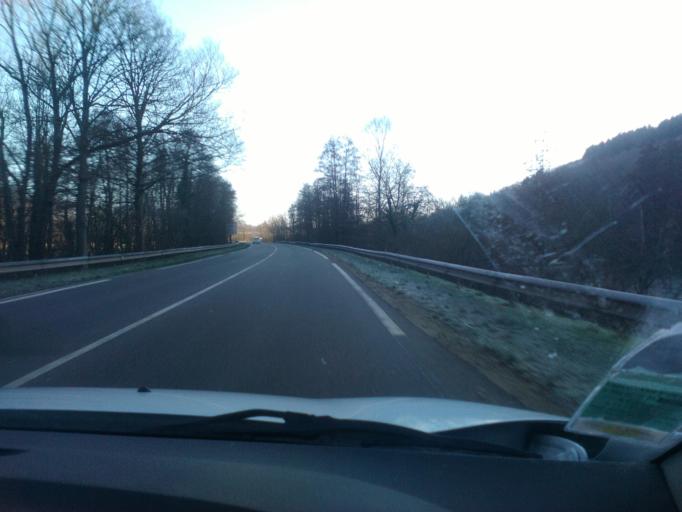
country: FR
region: Alsace
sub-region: Departement du Bas-Rhin
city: Russ
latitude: 48.4892
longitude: 7.2452
